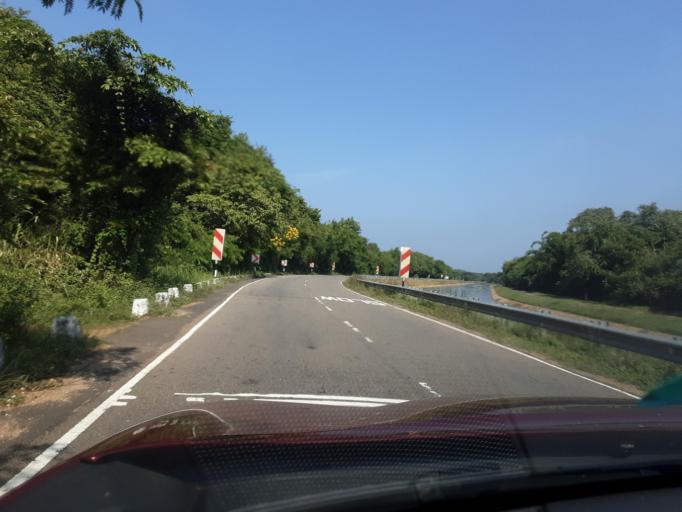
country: LK
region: Uva
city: Badulla
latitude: 7.2753
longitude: 81.0451
